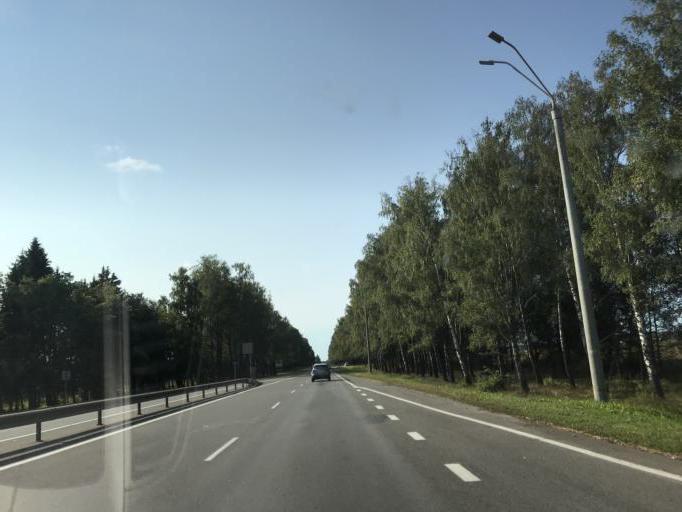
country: BY
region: Mogilev
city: Buynichy
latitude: 53.8487
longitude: 30.2522
